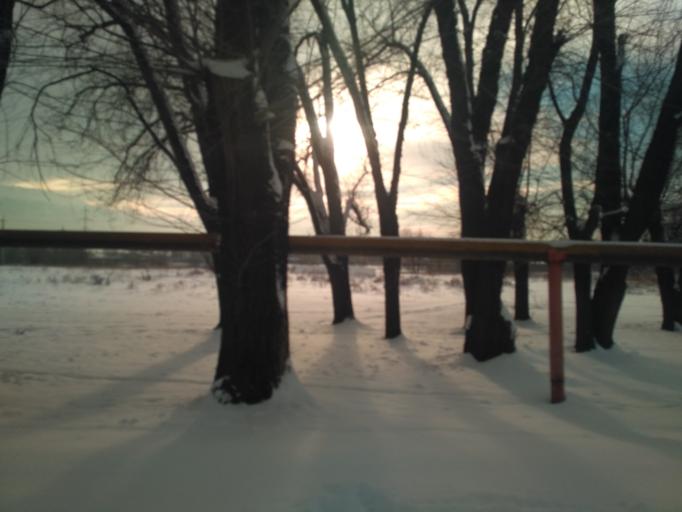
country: KZ
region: Almaty Qalasy
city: Almaty
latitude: 43.2167
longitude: 76.7716
